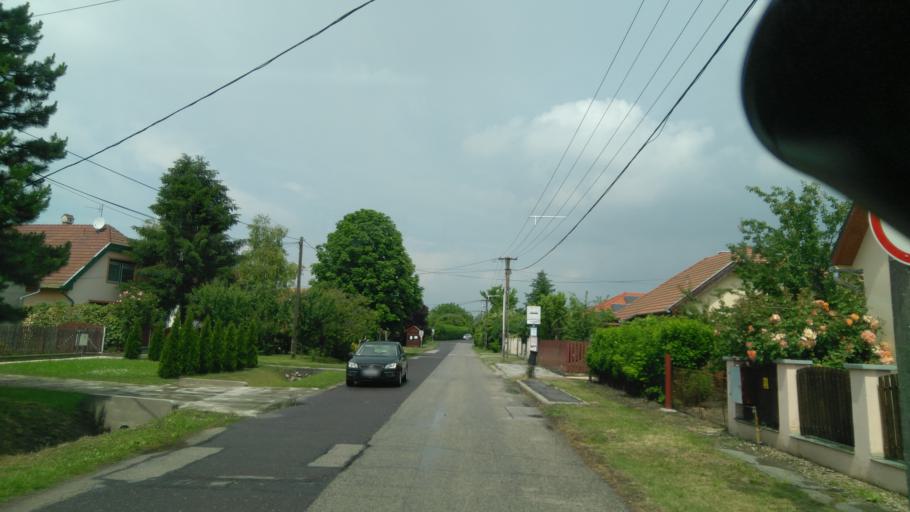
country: HU
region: Bekes
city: Bekescsaba
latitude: 46.6698
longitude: 21.1763
